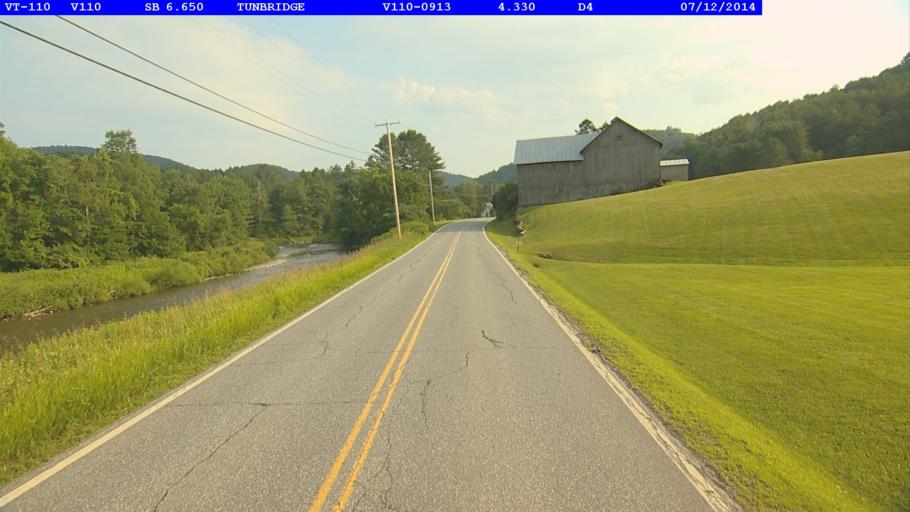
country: US
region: Vermont
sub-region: Orange County
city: Chelsea
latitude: 43.9072
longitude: -72.4831
